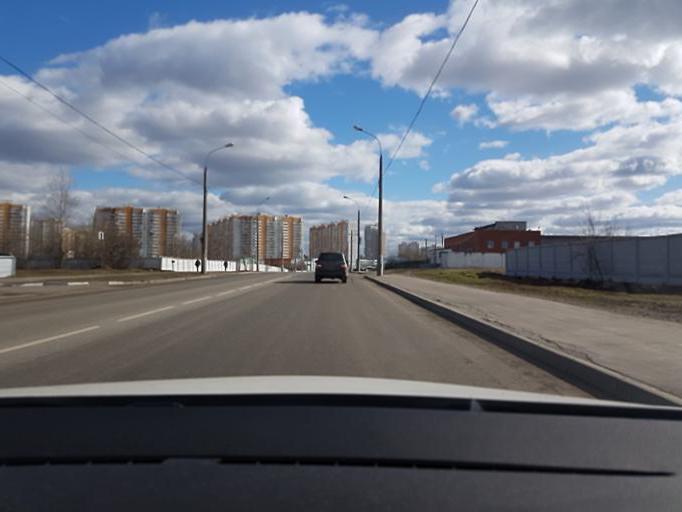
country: RU
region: Moskovskaya
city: Pavshino
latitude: 55.8369
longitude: 37.3446
